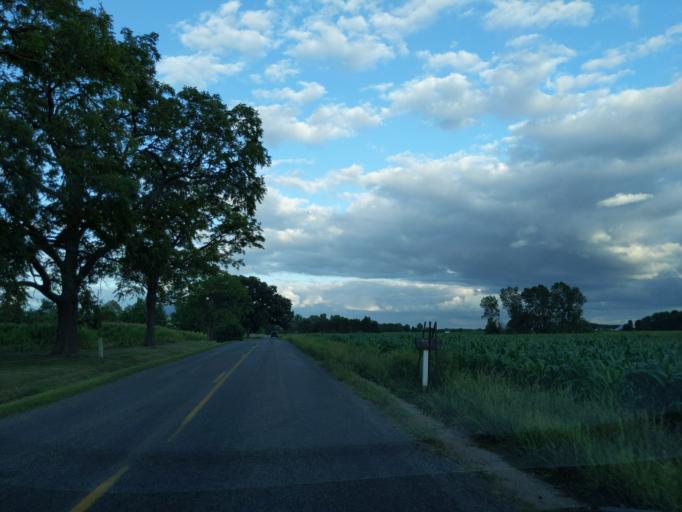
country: US
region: Michigan
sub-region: Ingham County
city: Holt
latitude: 42.5968
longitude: -84.5579
